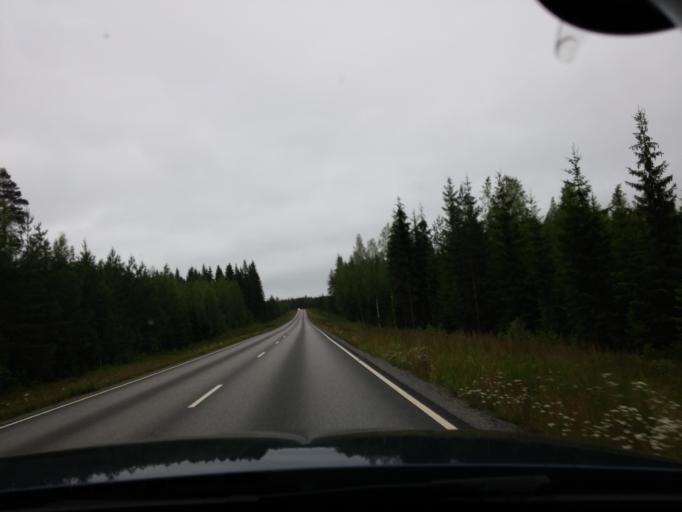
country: FI
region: Central Finland
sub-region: Saarijaervi-Viitasaari
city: Saarijaervi
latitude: 62.6789
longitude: 25.2065
